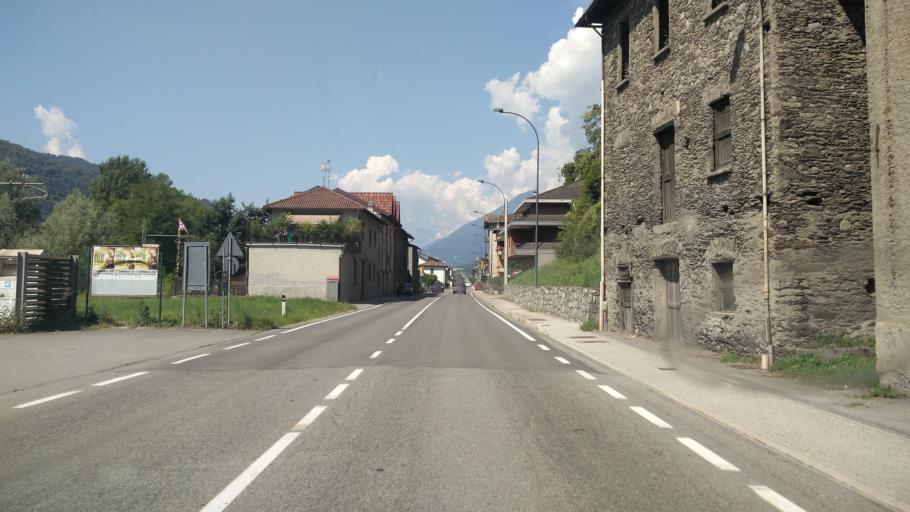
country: IT
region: Lombardy
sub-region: Provincia di Sondrio
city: San Giacomo
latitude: 46.1594
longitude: 10.0324
